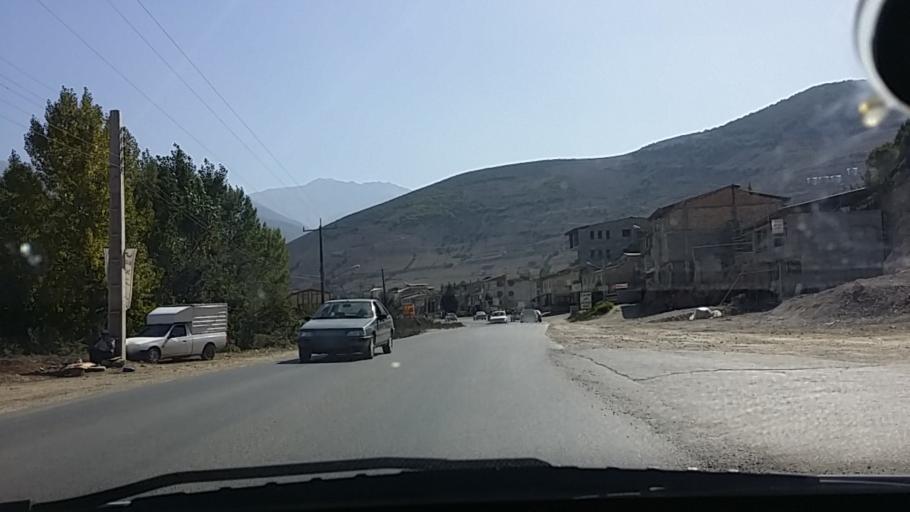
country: IR
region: Mazandaran
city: `Abbasabad
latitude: 36.5261
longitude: 51.1612
